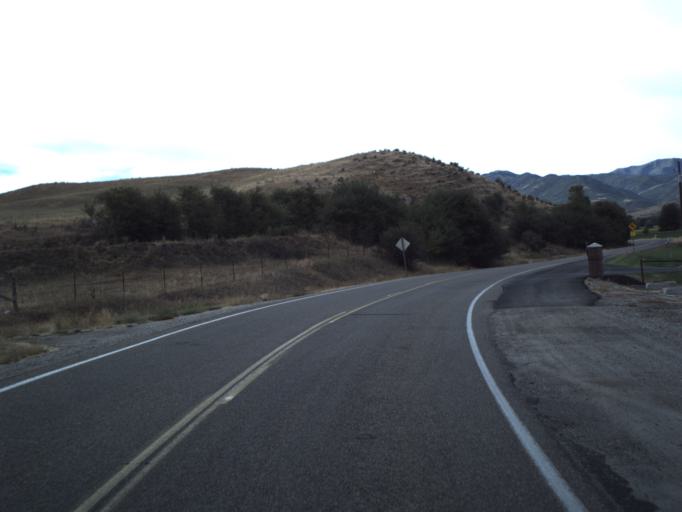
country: US
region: Utah
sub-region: Morgan County
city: Morgan
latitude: 41.0130
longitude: -111.6763
